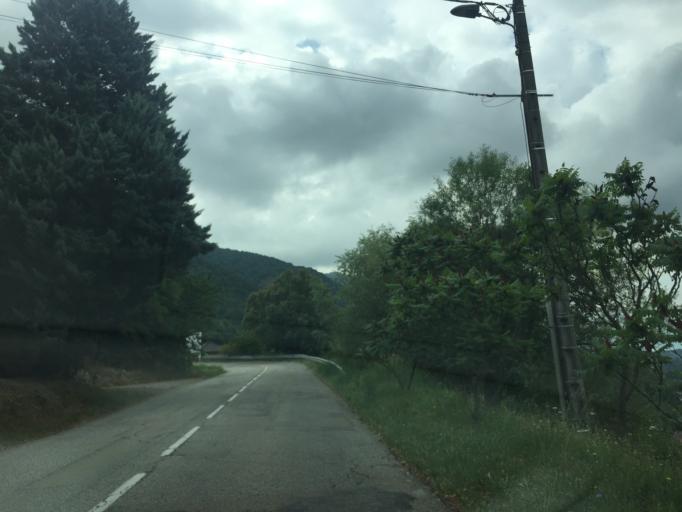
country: FR
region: Rhone-Alpes
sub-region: Departement de la Savoie
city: Barby
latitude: 45.5757
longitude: 5.9799
